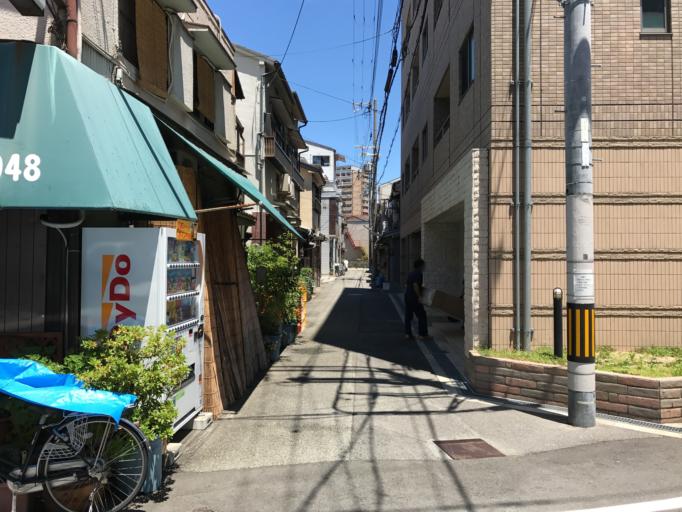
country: JP
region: Osaka
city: Osaka-shi
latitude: 34.6949
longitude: 135.4709
